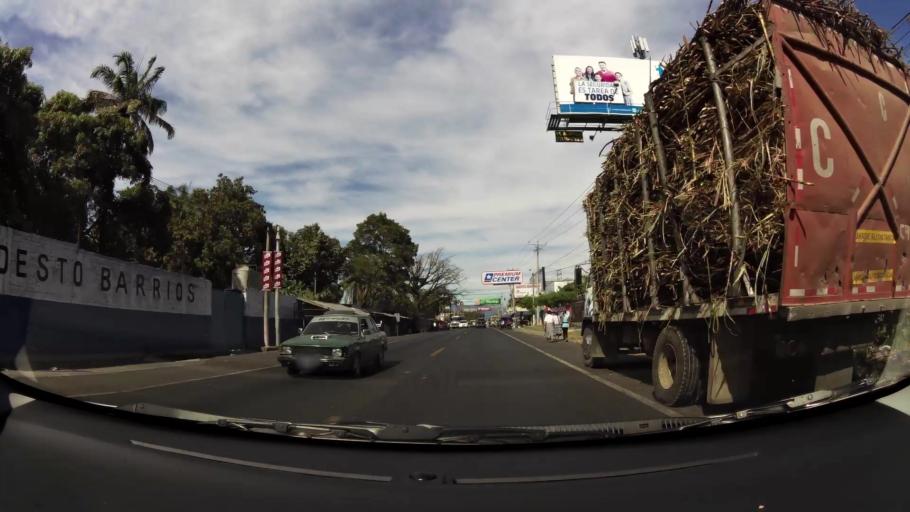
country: SV
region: San Salvador
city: Aguilares
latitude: 13.9560
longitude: -89.1852
